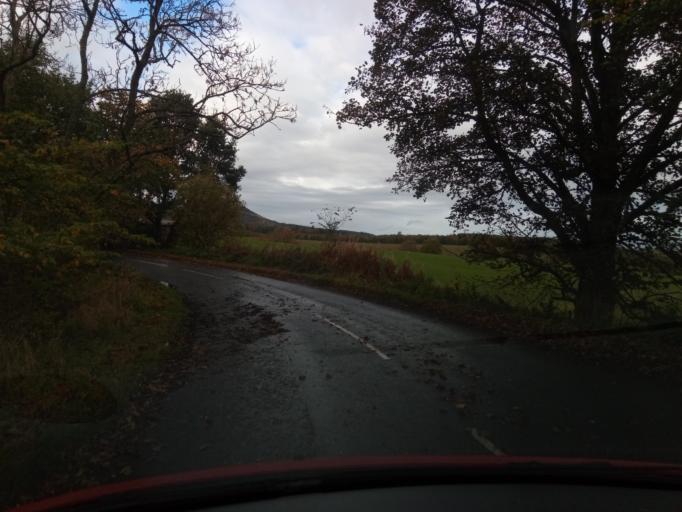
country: GB
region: Scotland
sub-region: The Scottish Borders
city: Newtown St Boswells
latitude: 55.5528
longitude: -2.7048
